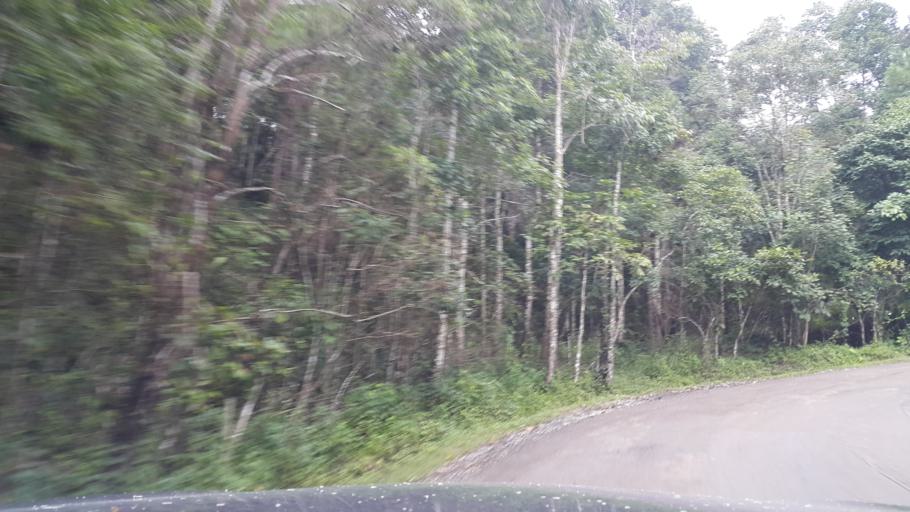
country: TH
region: Chiang Mai
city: Samoeng
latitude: 18.8828
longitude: 98.5258
